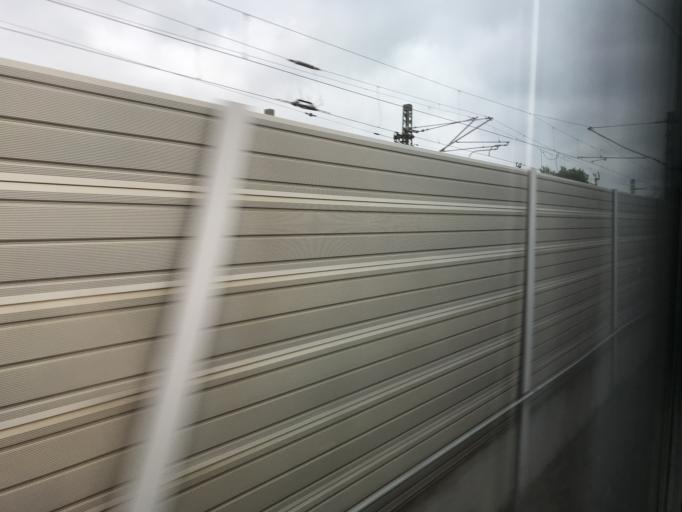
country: DE
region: Bavaria
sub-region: Upper Bavaria
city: Olching
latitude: 48.2112
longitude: 11.3297
